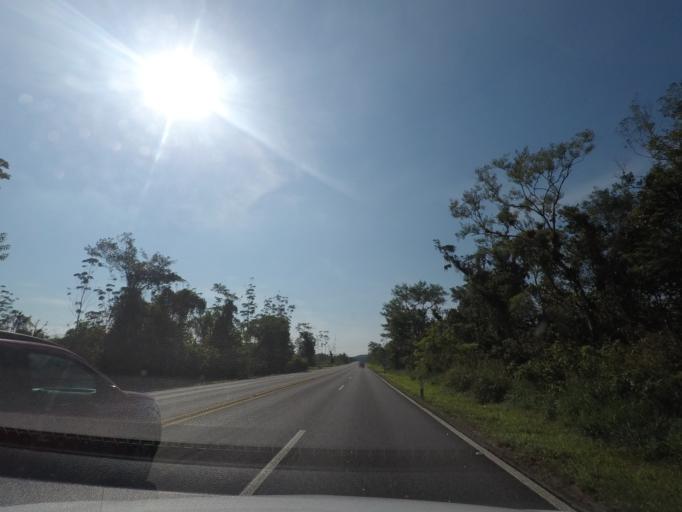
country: BR
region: Parana
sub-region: Paranagua
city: Paranagua
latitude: -25.5866
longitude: -48.6117
